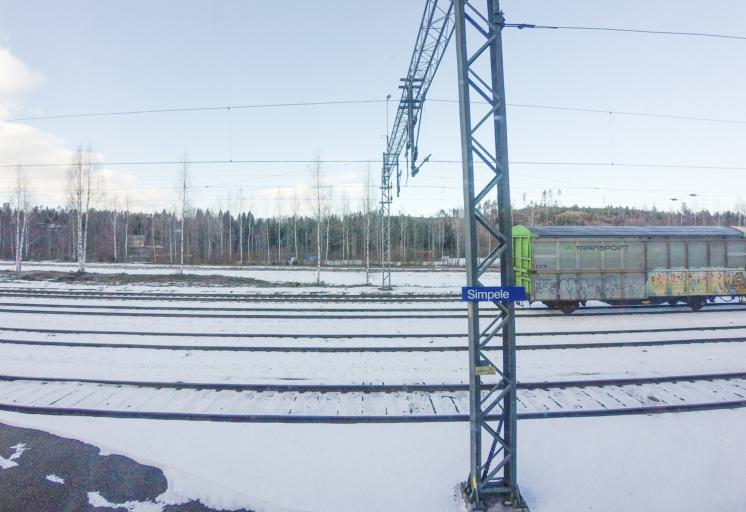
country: FI
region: South Karelia
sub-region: Imatra
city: Simpele
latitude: 61.4248
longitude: 29.3758
